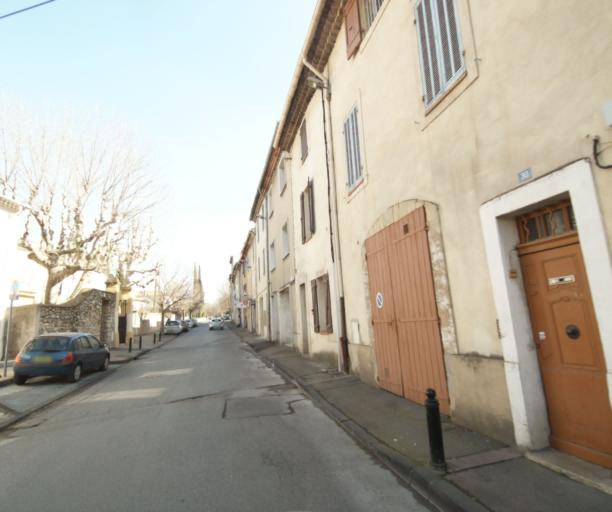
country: FR
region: Provence-Alpes-Cote d'Azur
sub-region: Departement des Bouches-du-Rhone
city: Gardanne
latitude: 43.4548
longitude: 5.4721
